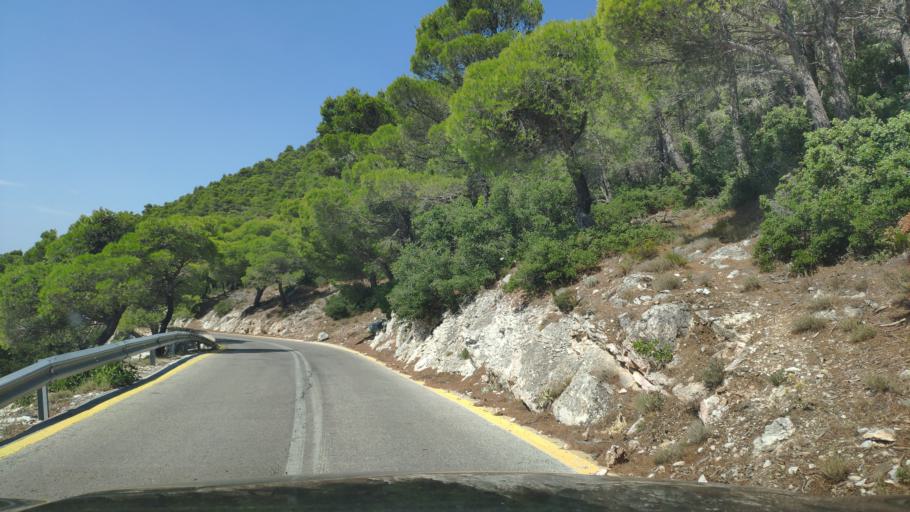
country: GR
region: Attica
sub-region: Nomarchia Anatolikis Attikis
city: Thrakomakedones
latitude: 38.1430
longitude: 23.7243
